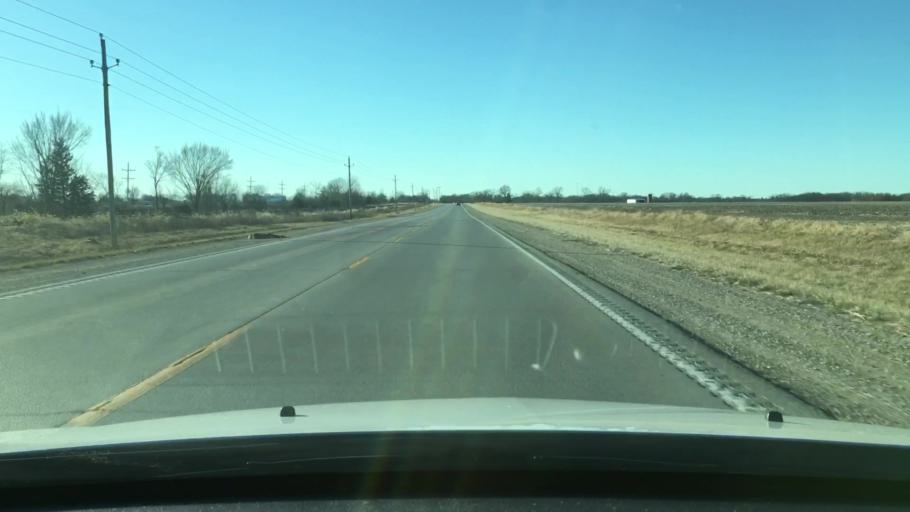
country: US
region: Missouri
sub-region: Audrain County
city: Mexico
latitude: 39.1878
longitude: -91.9643
